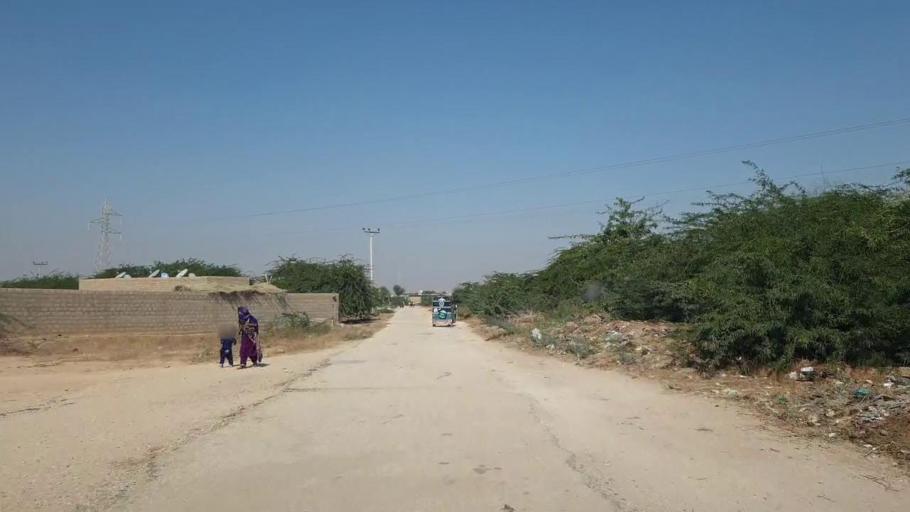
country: PK
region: Sindh
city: Jamshoro
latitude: 25.3535
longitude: 67.8312
